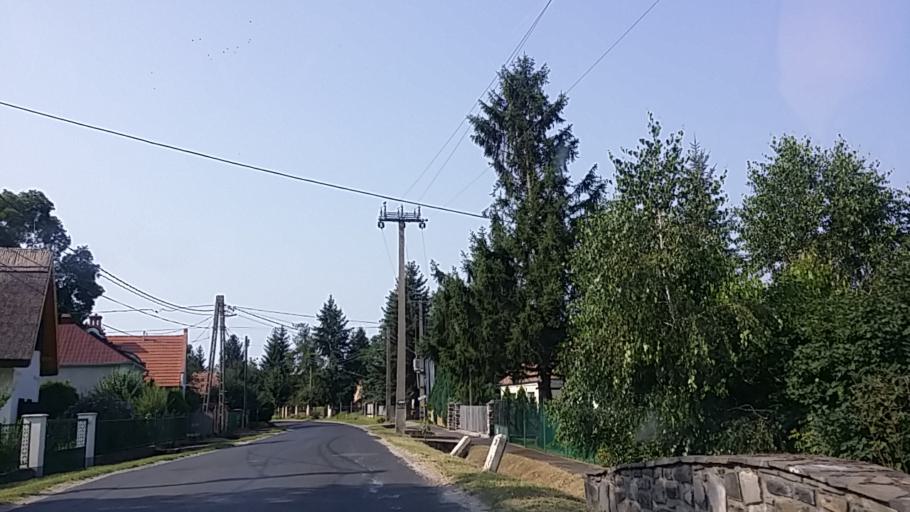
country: HU
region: Veszprem
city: Badacsonytomaj
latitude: 46.8147
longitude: 17.4743
